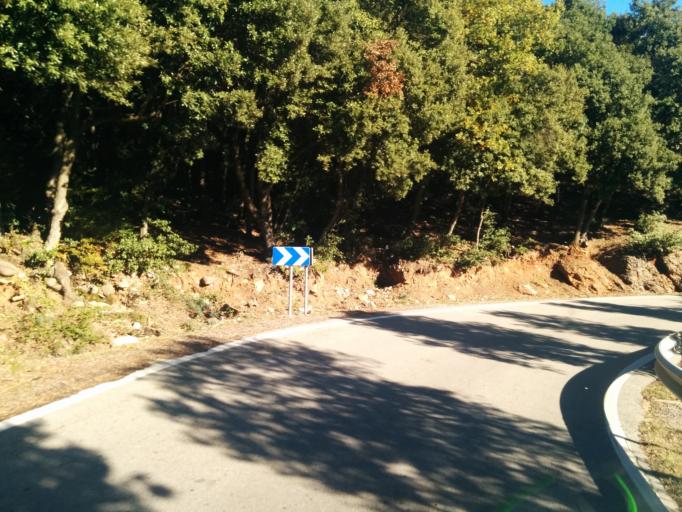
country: ES
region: Catalonia
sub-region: Provincia de Barcelona
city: Mura
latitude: 41.6531
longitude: 1.9805
